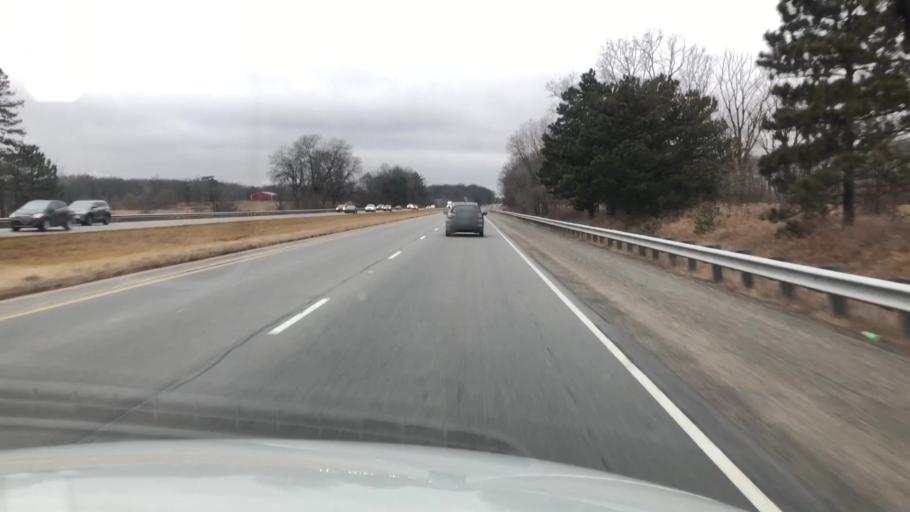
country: US
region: Indiana
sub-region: Whitley County
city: Churubusco
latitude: 41.1259
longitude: -85.3238
